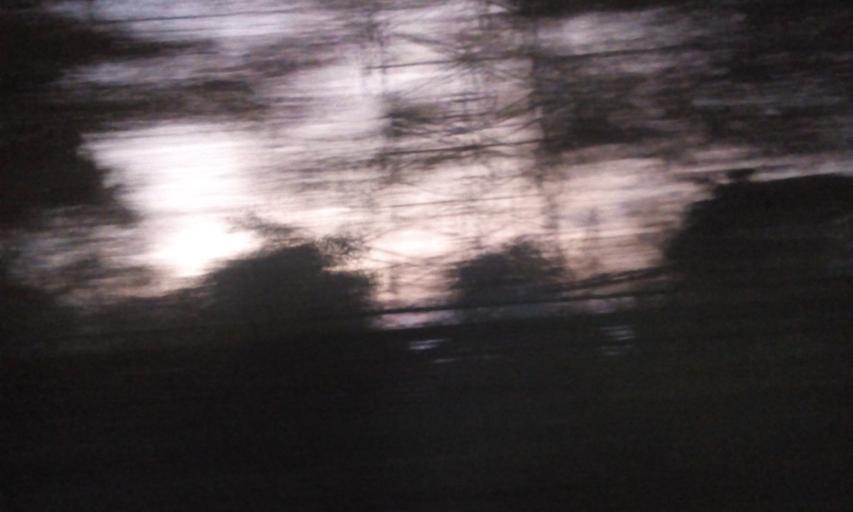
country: TH
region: Sing Buri
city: Sing Buri
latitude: 14.8444
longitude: 100.3920
